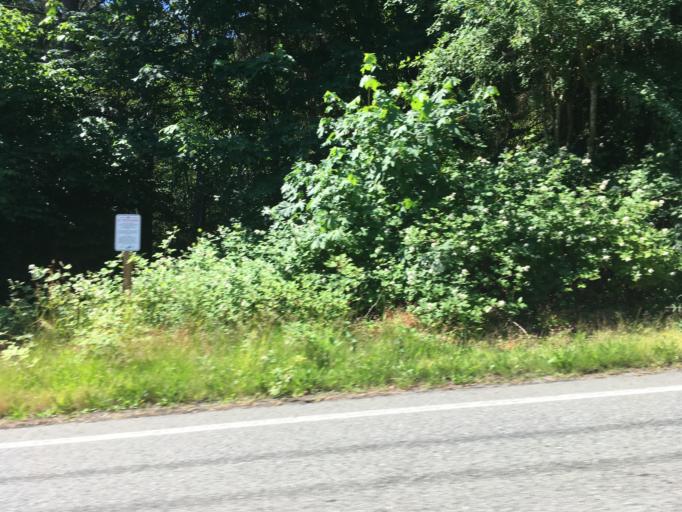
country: US
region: Washington
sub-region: King County
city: Bellevue
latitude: 47.6316
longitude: -122.1571
